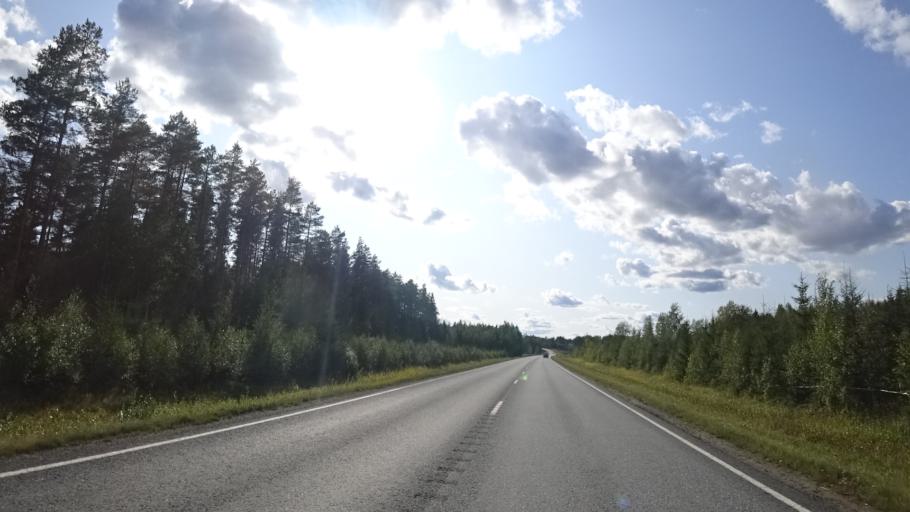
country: FI
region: North Karelia
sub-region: Keski-Karjala
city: Kitee
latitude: 62.0905
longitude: 30.0291
